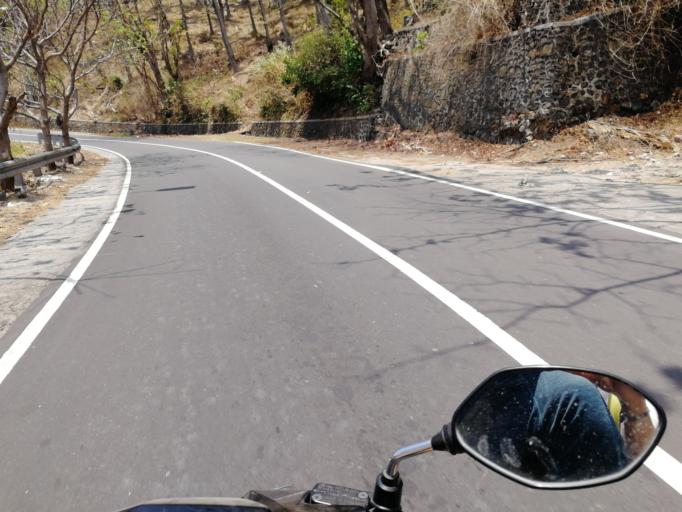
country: ID
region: West Nusa Tenggara
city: Karangsubagan
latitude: -8.4489
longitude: 116.0340
